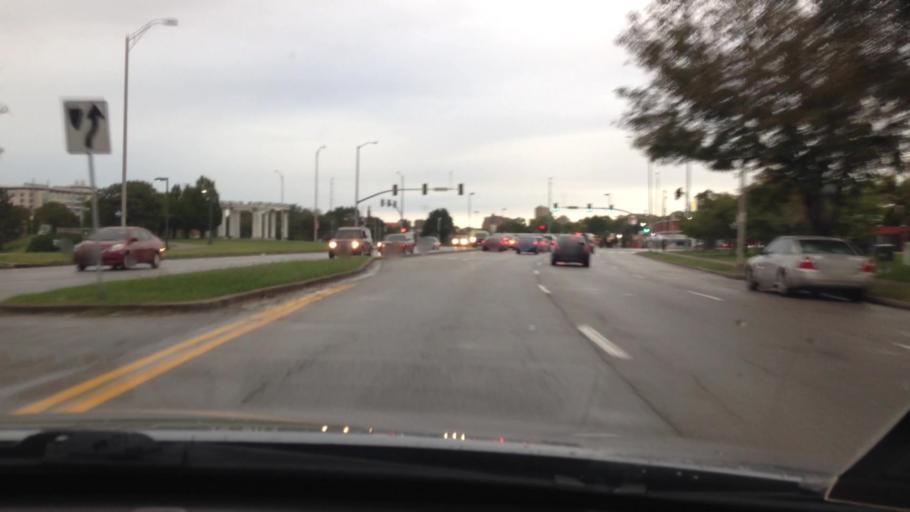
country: US
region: Kansas
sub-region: Johnson County
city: Westwood
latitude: 39.0419
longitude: -94.5668
